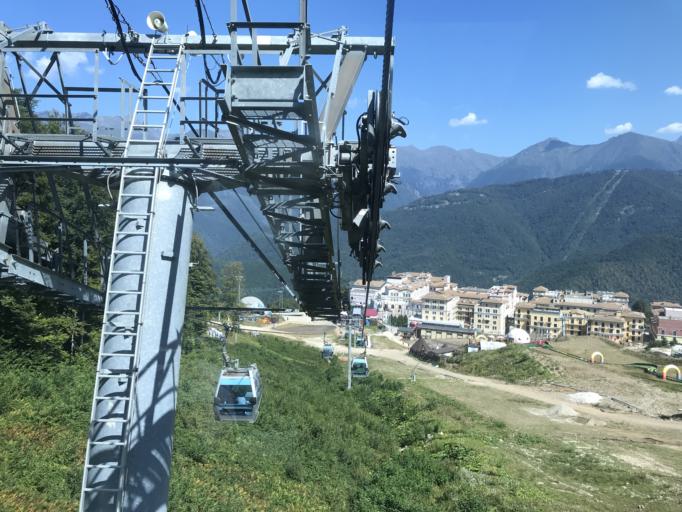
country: RU
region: Krasnodarskiy
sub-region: Sochi City
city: Krasnaya Polyana
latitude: 43.6660
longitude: 40.2566
